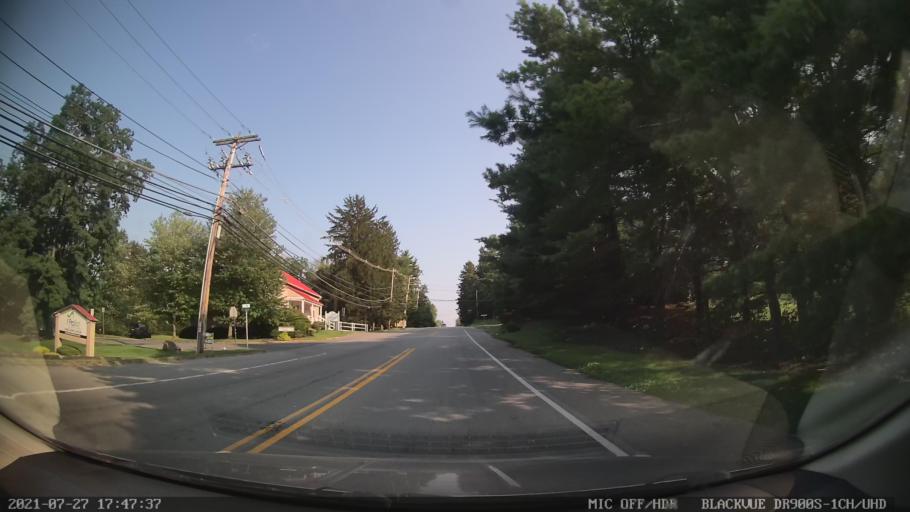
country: US
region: Pennsylvania
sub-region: Berks County
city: Muhlenberg Park
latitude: 40.3640
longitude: -75.9545
